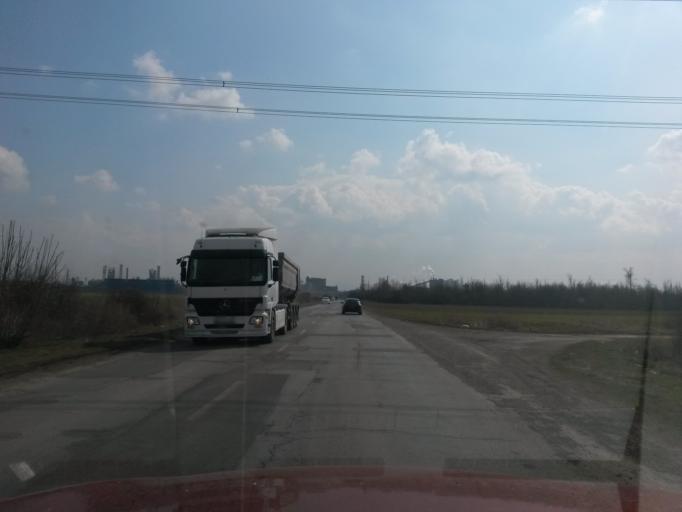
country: SK
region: Kosicky
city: Kosice
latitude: 48.6247
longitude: 21.1740
